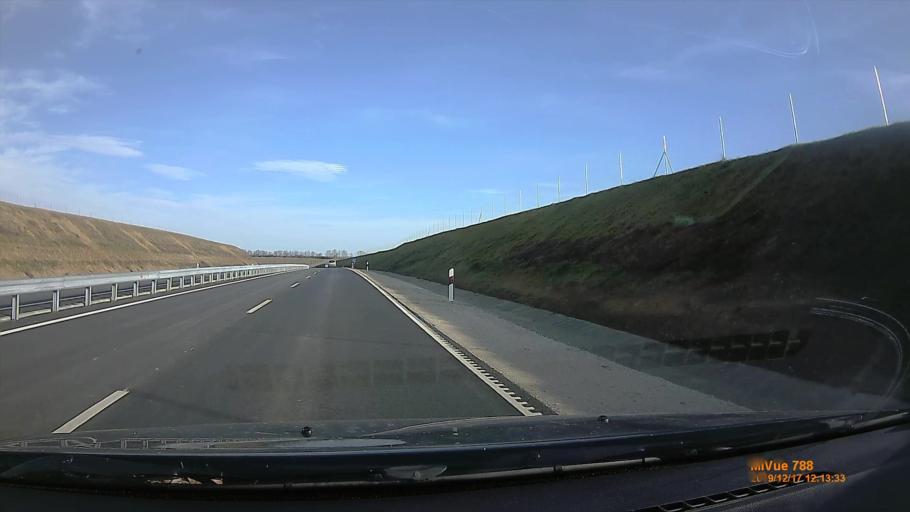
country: HU
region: Somogy
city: Kaposvar
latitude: 46.4553
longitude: 17.7792
